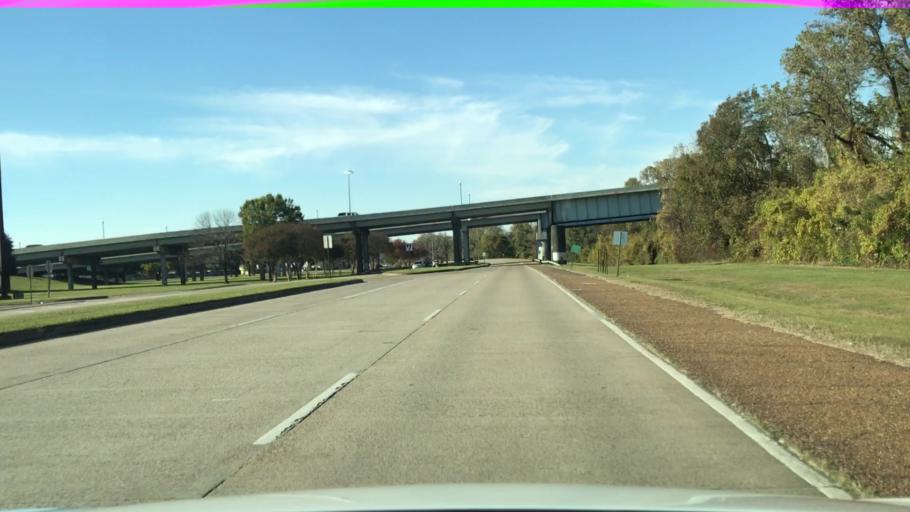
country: US
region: Louisiana
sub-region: Bossier Parish
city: Bossier City
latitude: 32.4897
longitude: -93.6995
